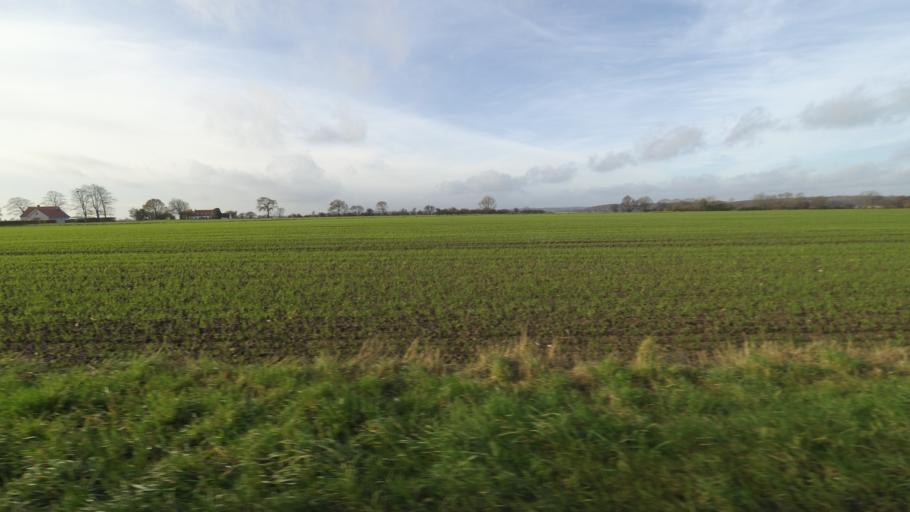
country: DK
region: Central Jutland
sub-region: Odder Kommune
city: Odder
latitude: 55.9537
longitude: 10.2368
